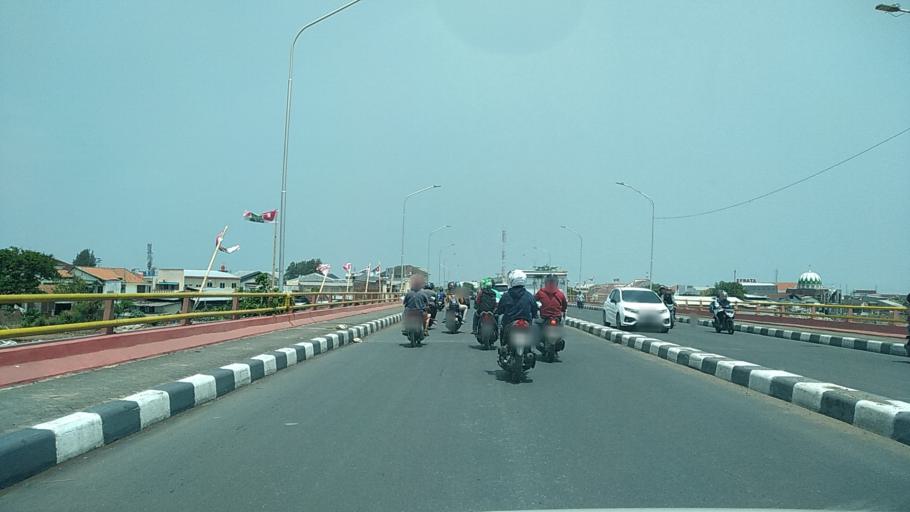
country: ID
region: Central Java
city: Semarang
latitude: -6.9733
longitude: 110.4431
